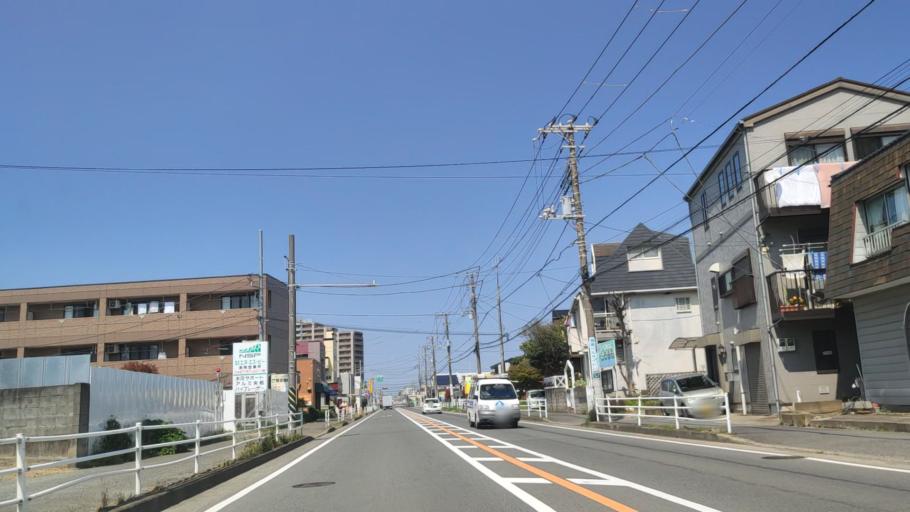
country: JP
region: Kanagawa
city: Chigasaki
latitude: 35.3279
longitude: 139.3767
